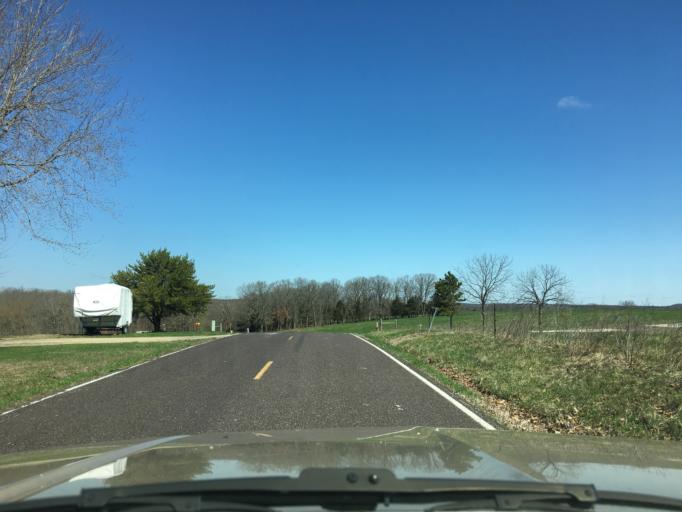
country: US
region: Missouri
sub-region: Franklin County
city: New Haven
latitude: 38.5391
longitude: -91.3289
